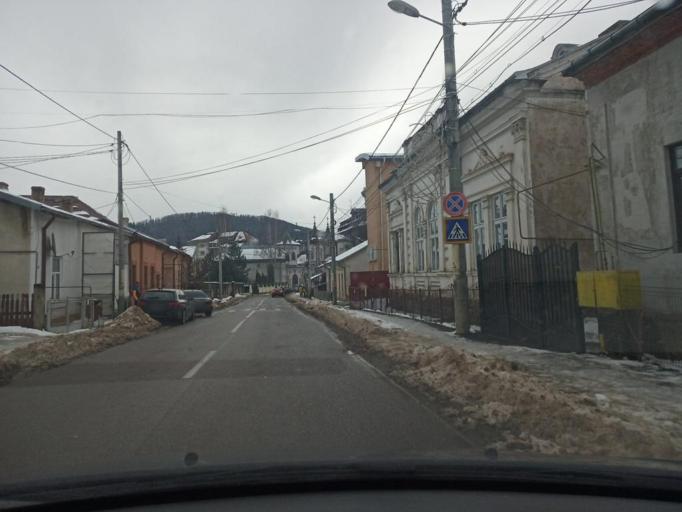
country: RO
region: Suceava
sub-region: Oras Gura Humorului
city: Gura Humorului
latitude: 47.5571
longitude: 25.8902
